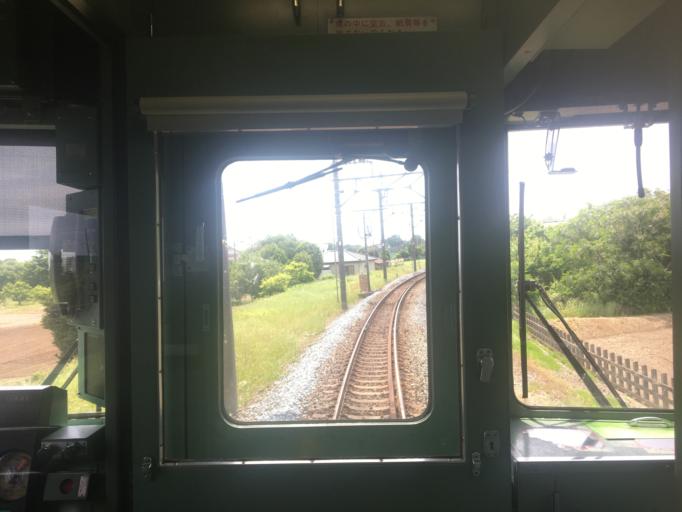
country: JP
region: Saitama
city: Morohongo
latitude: 35.9365
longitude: 139.3488
